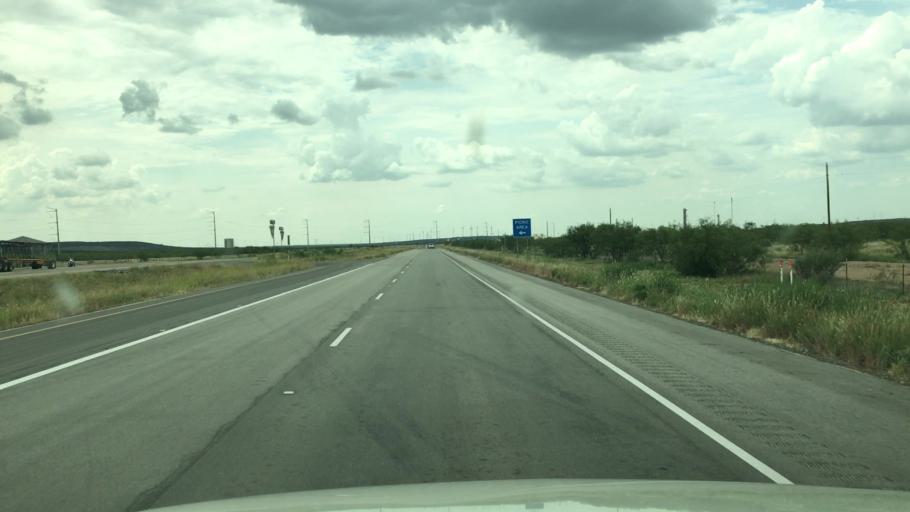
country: US
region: Texas
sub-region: Glasscock County
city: Garden City
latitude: 31.9655
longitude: -101.2285
